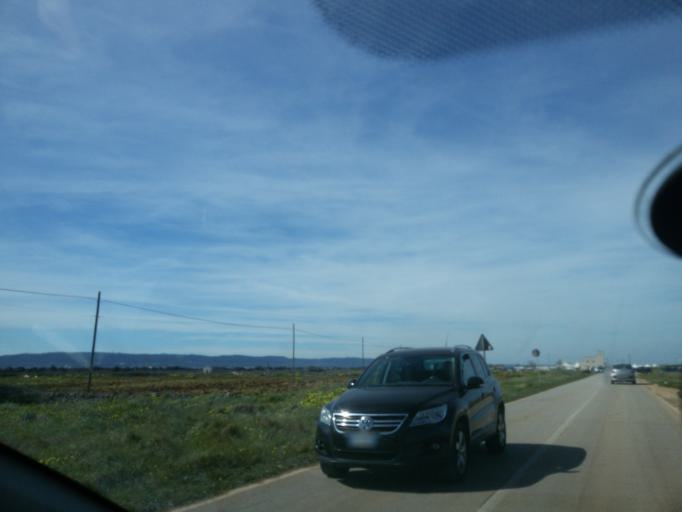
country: IT
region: Apulia
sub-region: Provincia di Brindisi
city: Pezze di Greco
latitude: 40.8519
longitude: 17.4496
